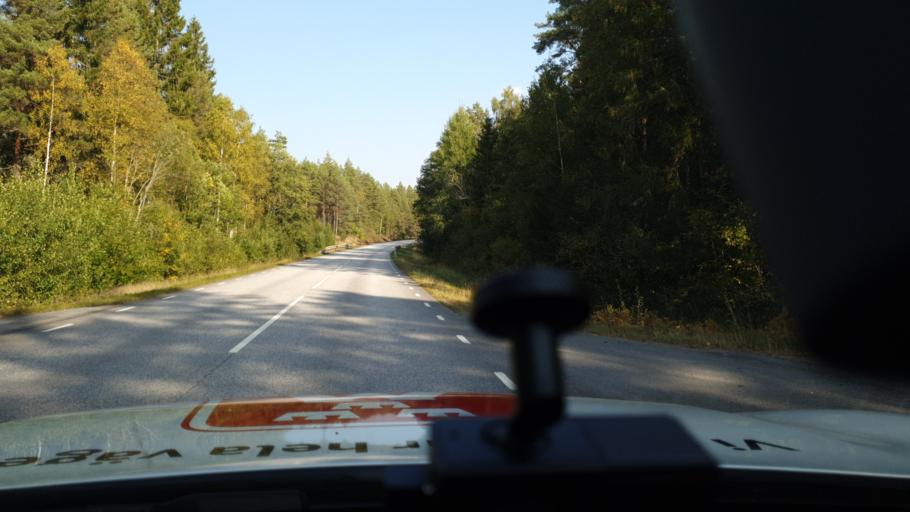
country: SE
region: Kalmar
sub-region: Vimmerby Kommun
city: Vimmerby
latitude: 57.5922
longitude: 16.0125
